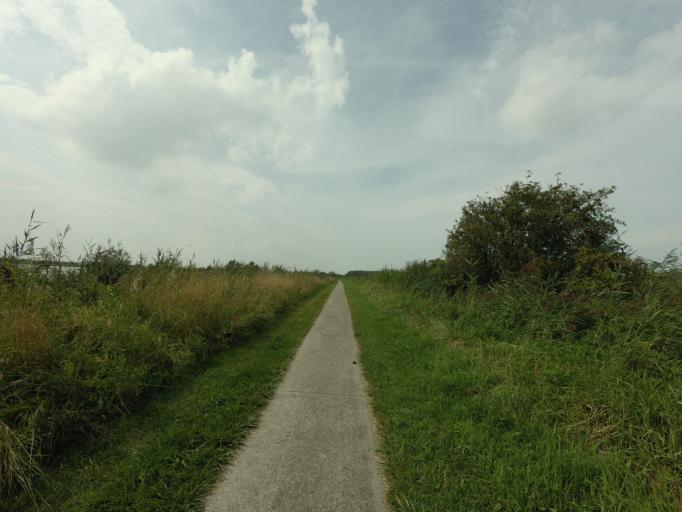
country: NL
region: Flevoland
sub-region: Gemeente Almere
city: Almere Stad
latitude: 52.4007
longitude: 5.2006
